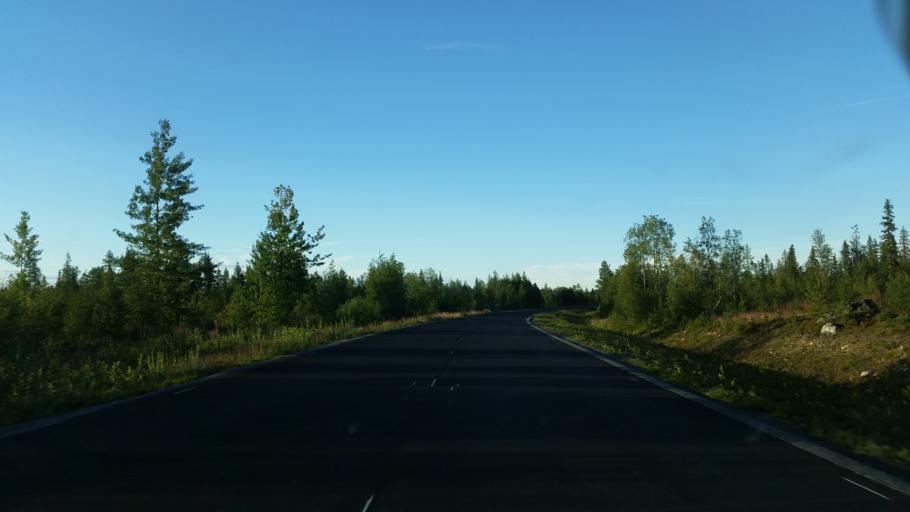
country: SE
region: Vaesterbotten
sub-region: Dorotea Kommun
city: Dorotea
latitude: 64.3186
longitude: 16.6114
